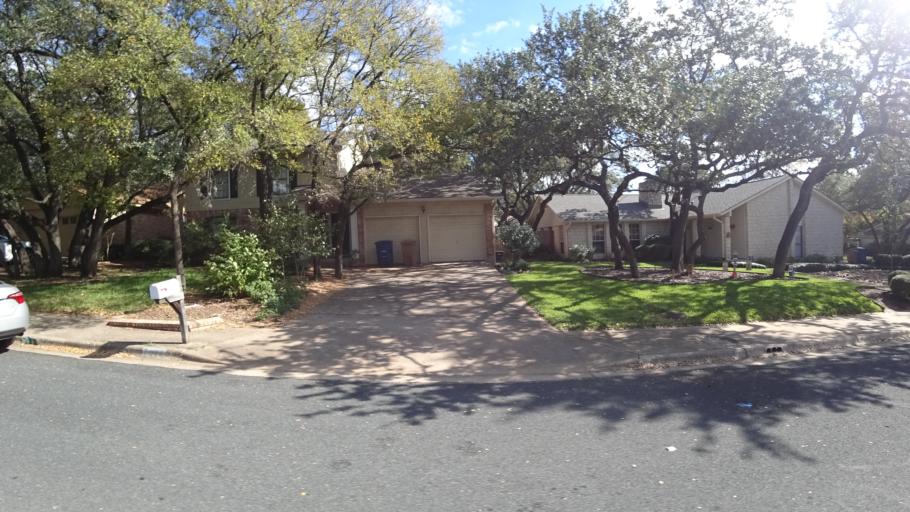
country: US
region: Texas
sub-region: Williamson County
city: Jollyville
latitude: 30.4169
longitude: -97.7277
